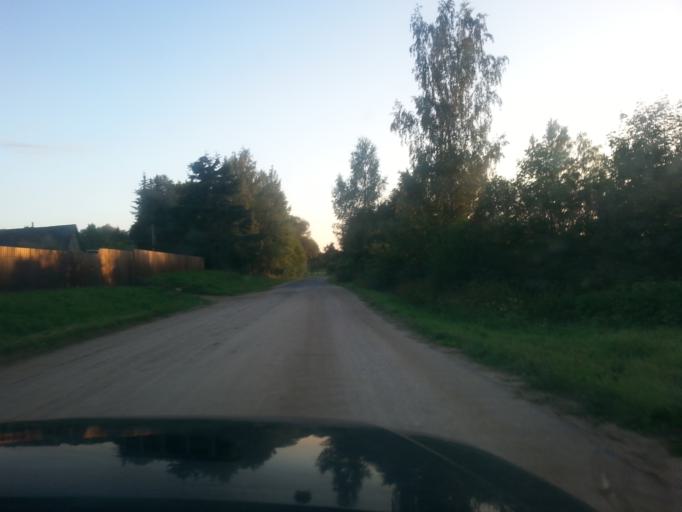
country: BY
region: Minsk
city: Narach
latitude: 54.9773
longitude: 26.6449
